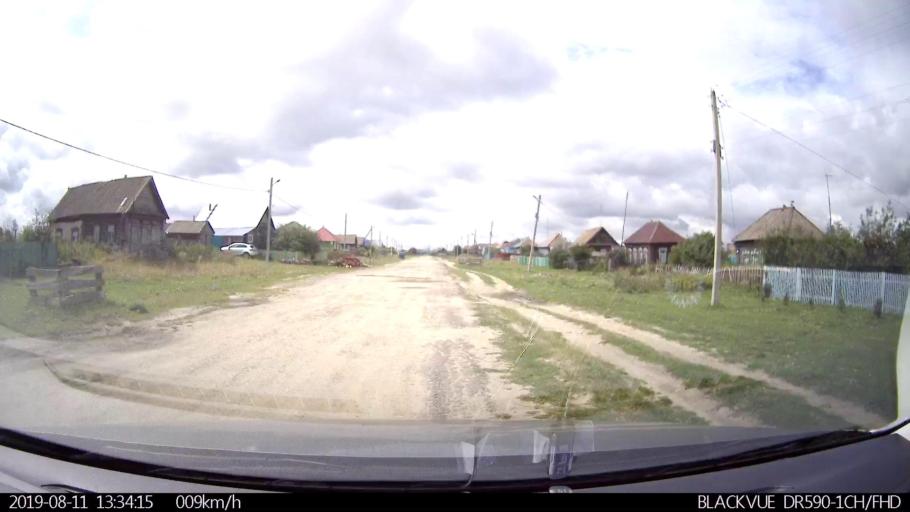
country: RU
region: Ulyanovsk
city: Ignatovka
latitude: 53.8596
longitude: 47.5931
